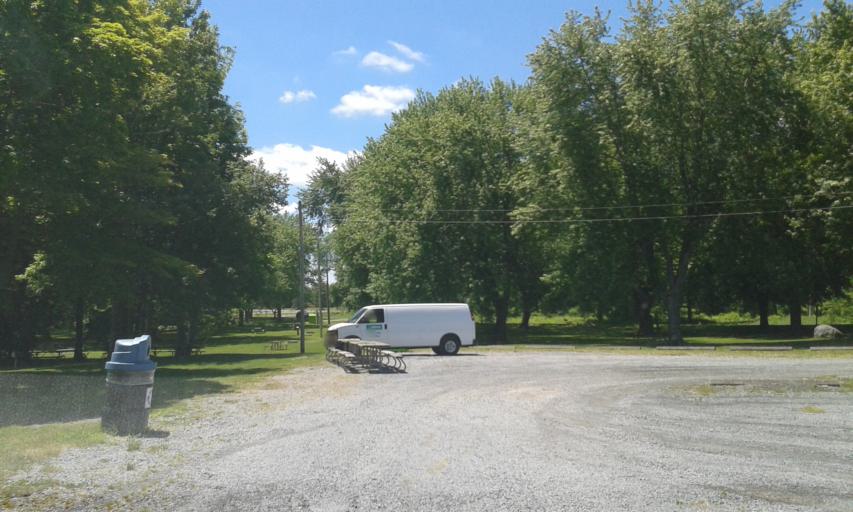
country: US
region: New York
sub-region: St. Lawrence County
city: Massena
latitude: 45.0164
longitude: -74.8903
